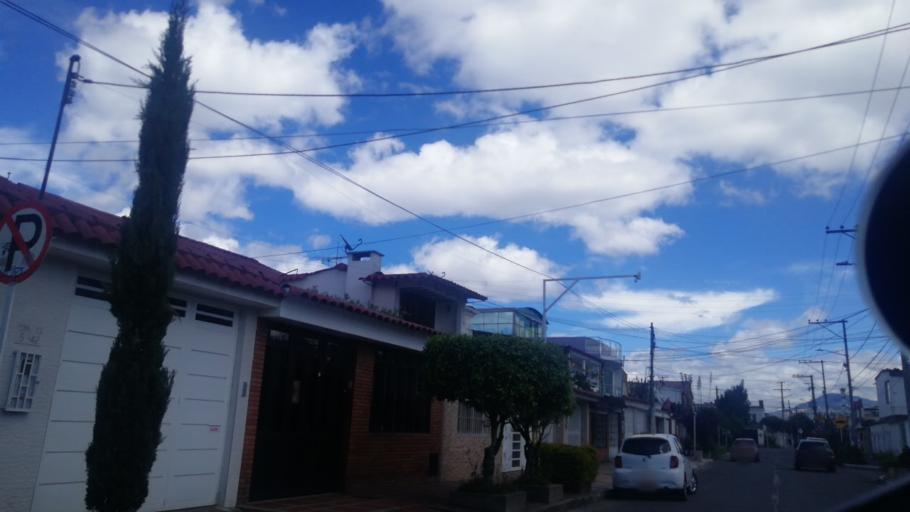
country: CO
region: Bogota D.C.
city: Bogota
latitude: 4.6288
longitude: -74.1409
